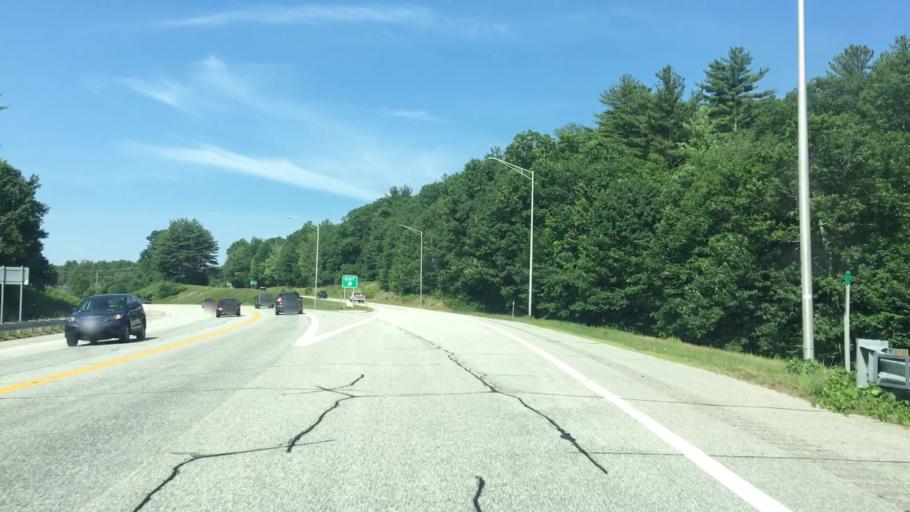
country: US
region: New Hampshire
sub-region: Merrimack County
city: Henniker
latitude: 43.1900
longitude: -71.8222
